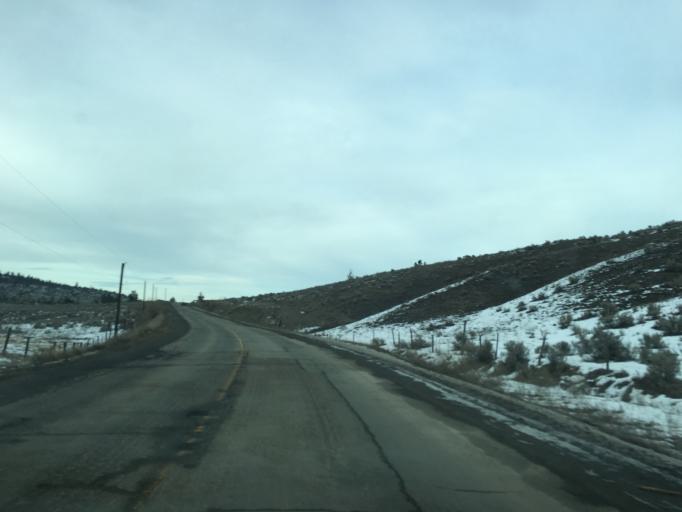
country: CA
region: British Columbia
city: Kamloops
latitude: 50.6194
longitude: -120.4425
